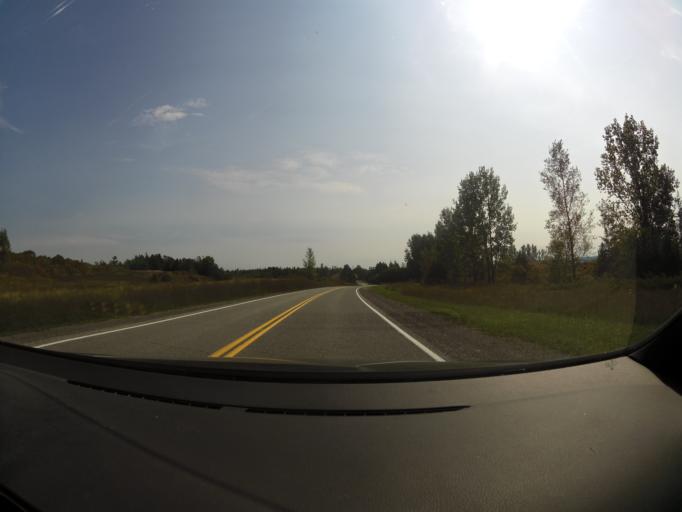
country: CA
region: Ontario
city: Arnprior
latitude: 45.3400
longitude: -76.1930
